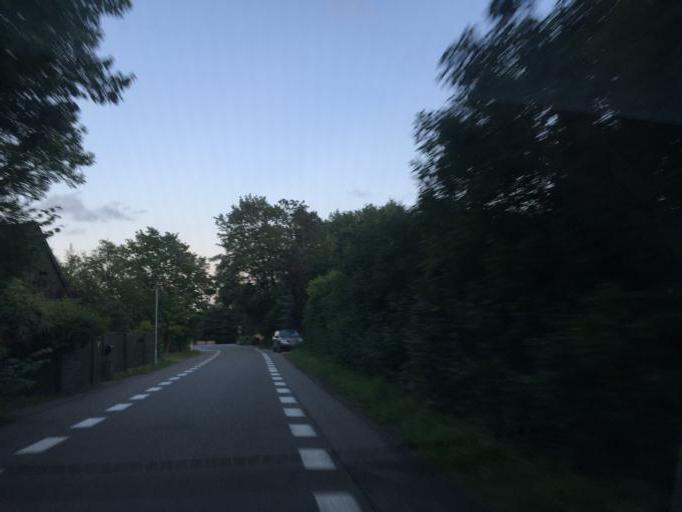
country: DK
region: Zealand
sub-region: Solrod Kommune
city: Havdrup
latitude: 55.5160
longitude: 12.1442
